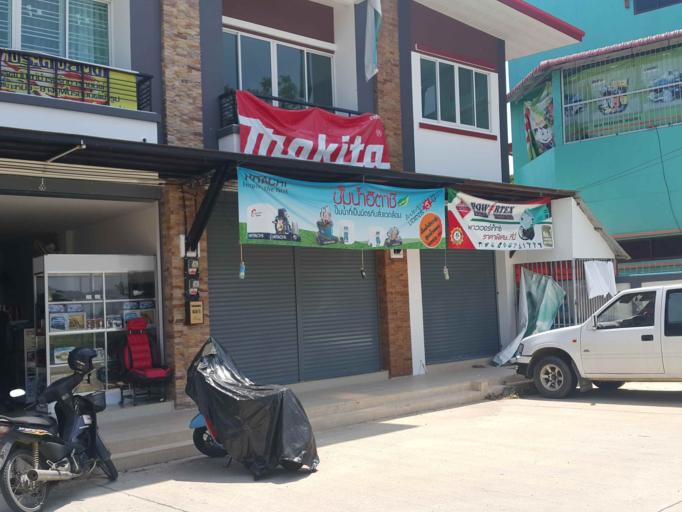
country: TH
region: Chiang Mai
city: San Sai
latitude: 18.8364
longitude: 99.0311
